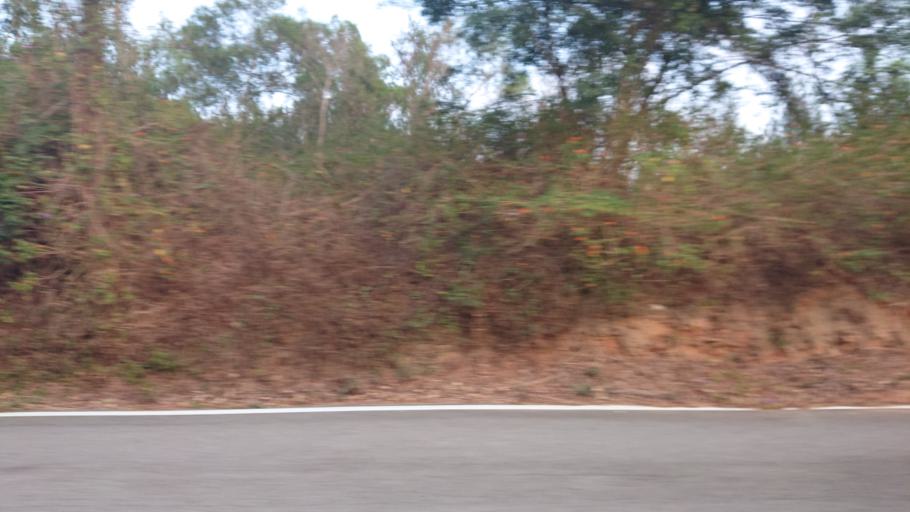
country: CN
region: Fujian
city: Dadeng
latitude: 24.4879
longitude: 118.4405
